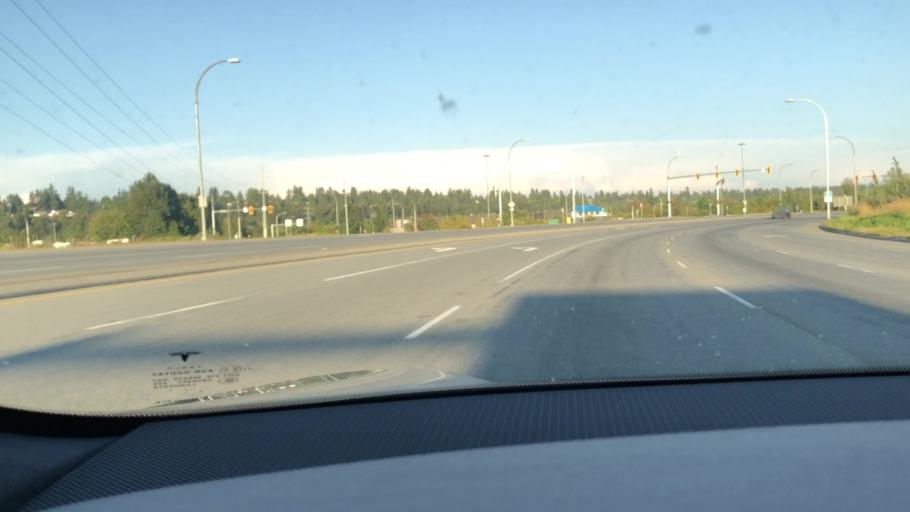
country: CA
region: British Columbia
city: Delta
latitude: 49.1472
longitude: -122.9455
